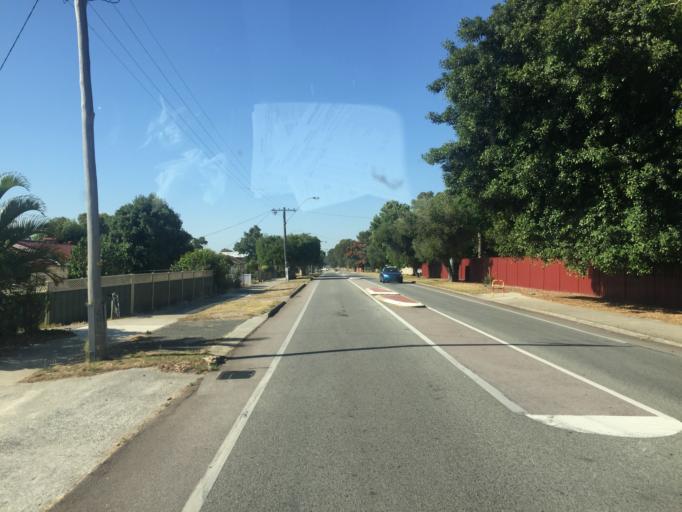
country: AU
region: Western Australia
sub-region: Gosnells
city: Maddington
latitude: -32.0363
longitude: 115.9821
